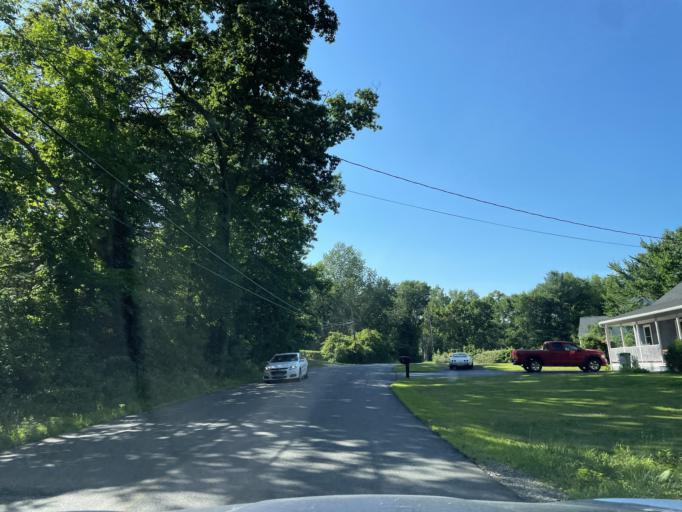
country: US
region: Massachusetts
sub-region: Worcester County
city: Charlton
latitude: 42.1623
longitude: -72.0228
